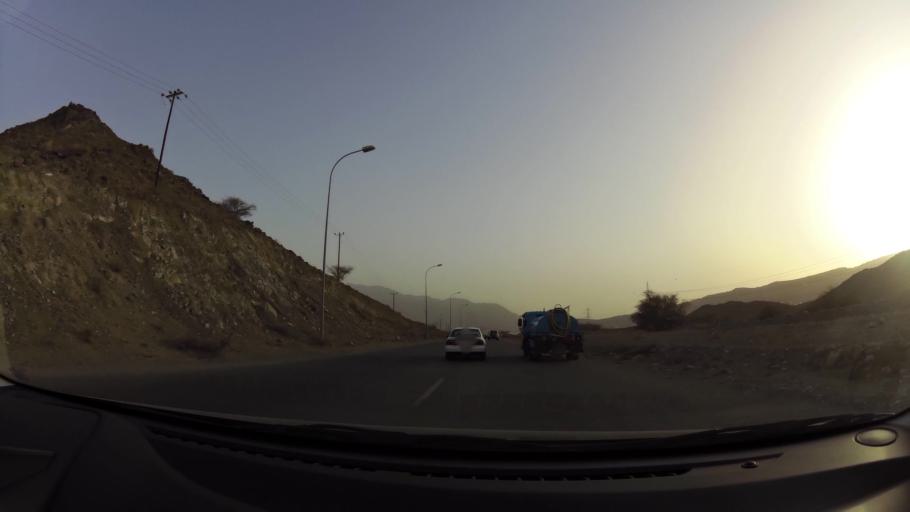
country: OM
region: Muhafazat Masqat
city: Bawshar
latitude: 23.4963
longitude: 58.3243
